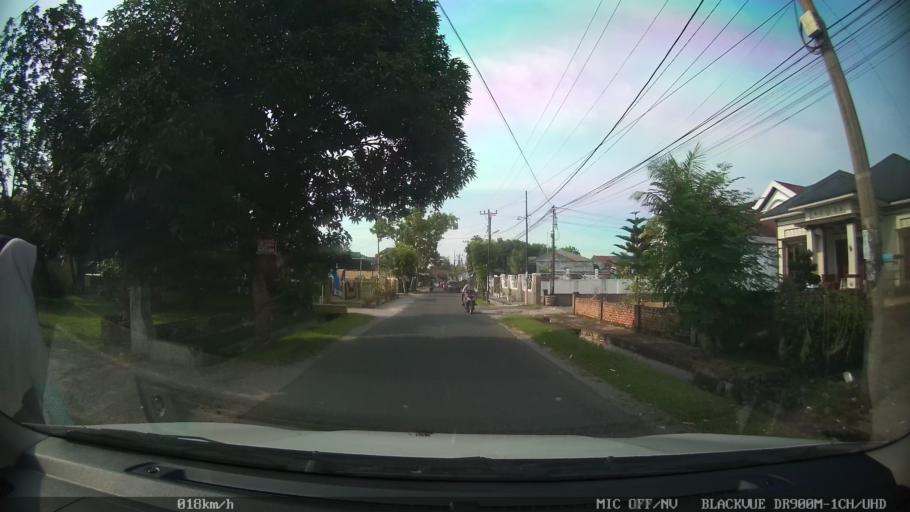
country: ID
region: North Sumatra
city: Binjai
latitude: 3.6070
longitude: 98.5112
